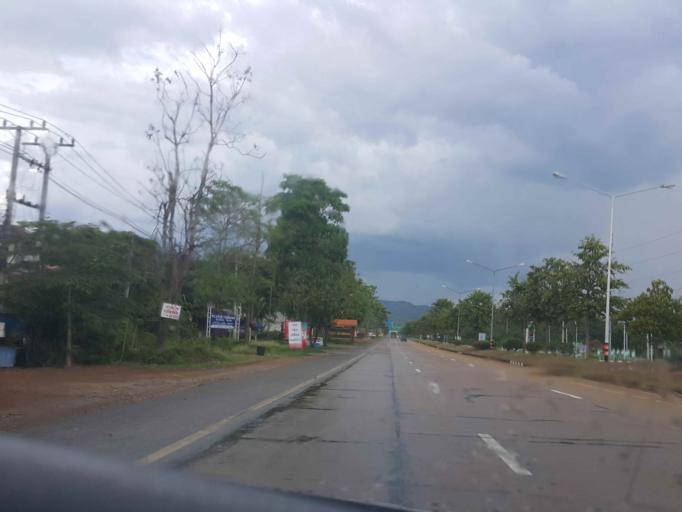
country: TH
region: Phrae
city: Den Chai
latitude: 17.9757
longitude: 100.0847
